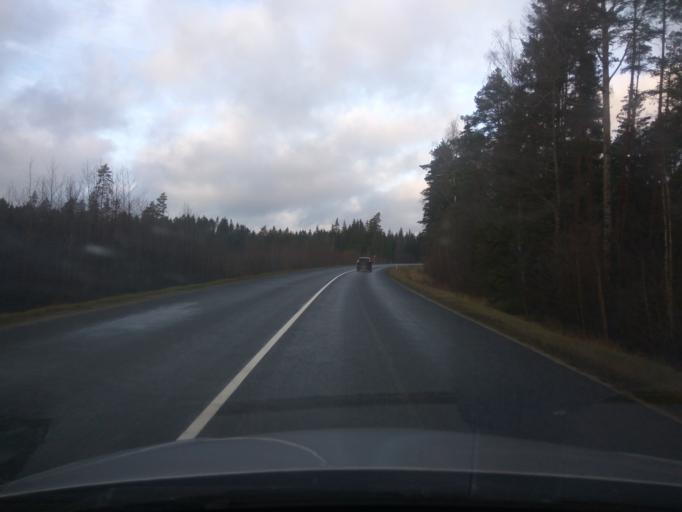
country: LV
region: Skrunda
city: Skrunda
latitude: 56.8559
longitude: 22.1508
